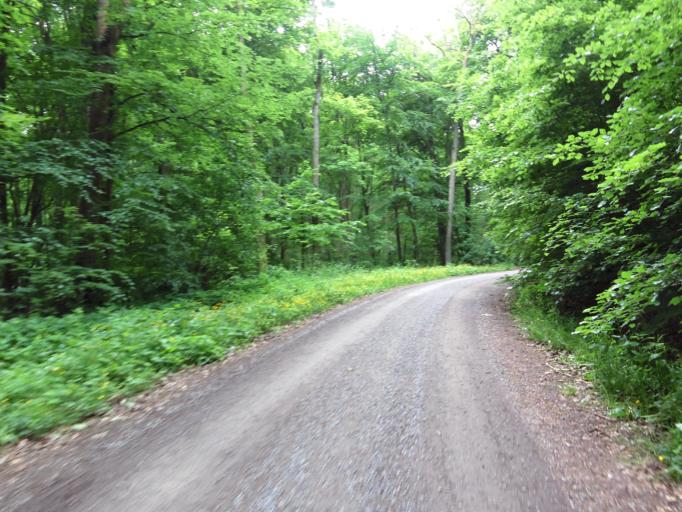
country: DE
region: Bavaria
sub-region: Regierungsbezirk Unterfranken
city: Wuerzburg
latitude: 49.7671
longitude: 9.8960
